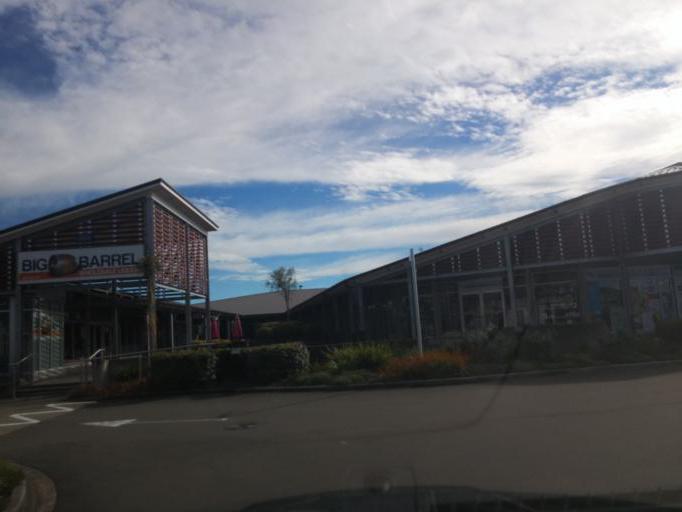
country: NZ
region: Manawatu-Wanganui
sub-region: Palmerston North City
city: Palmerston North
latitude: -40.3876
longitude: 175.6386
